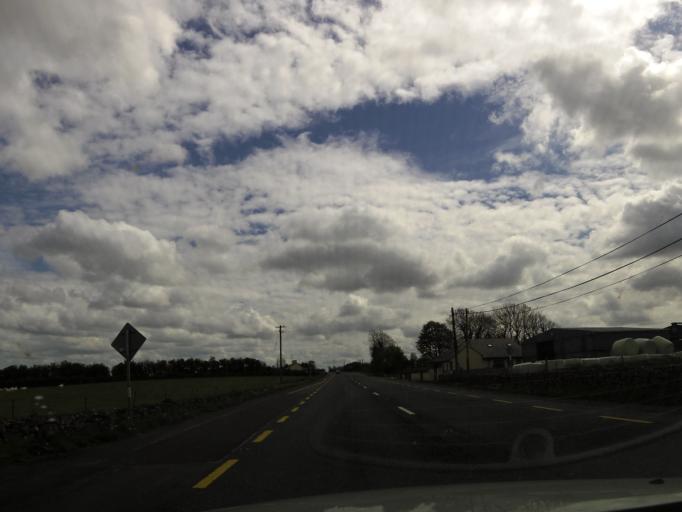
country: IE
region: Connaught
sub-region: County Galway
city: Tuam
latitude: 53.5814
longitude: -8.8545
